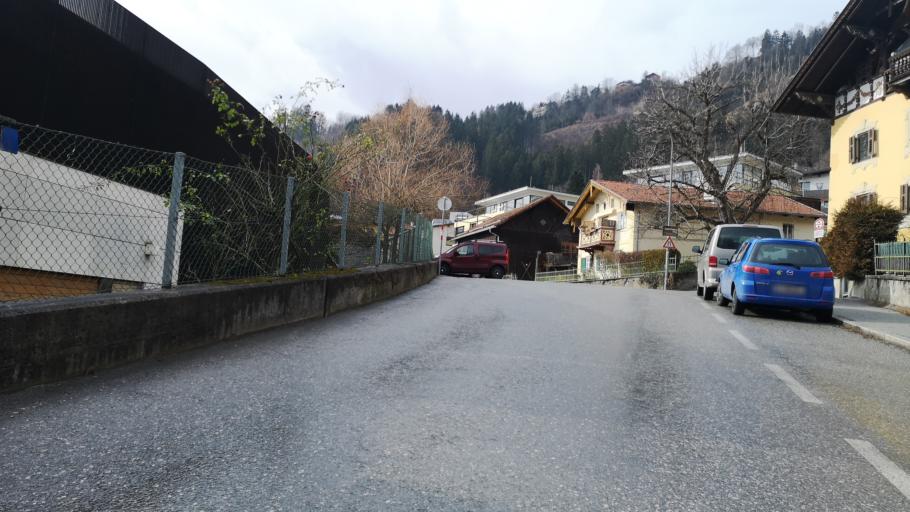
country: AT
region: Tyrol
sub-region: Innsbruck Stadt
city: Innsbruck
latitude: 47.2843
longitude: 11.4093
